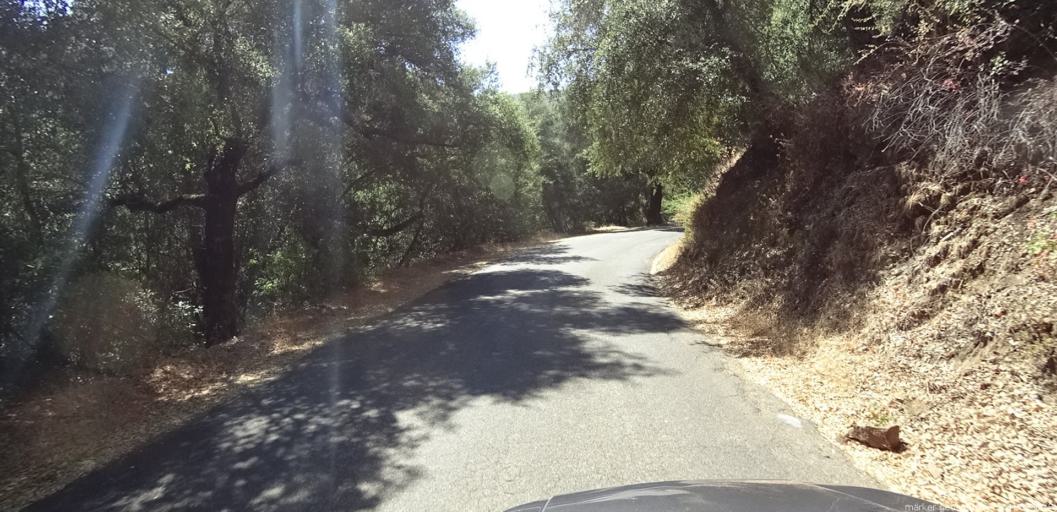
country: US
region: California
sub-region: Monterey County
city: Greenfield
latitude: 36.0134
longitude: -121.4202
